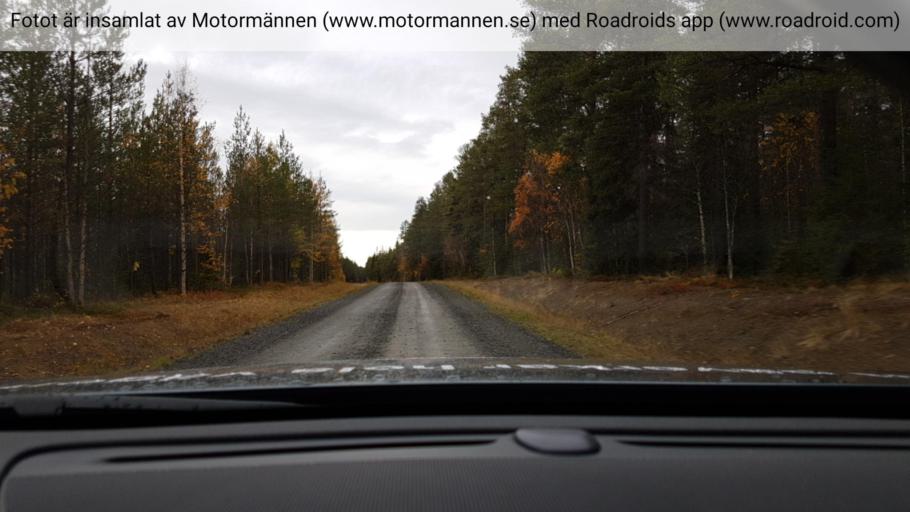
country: SE
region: Norrbotten
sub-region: Pajala Kommun
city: Pajala
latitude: 67.1239
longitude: 22.6802
